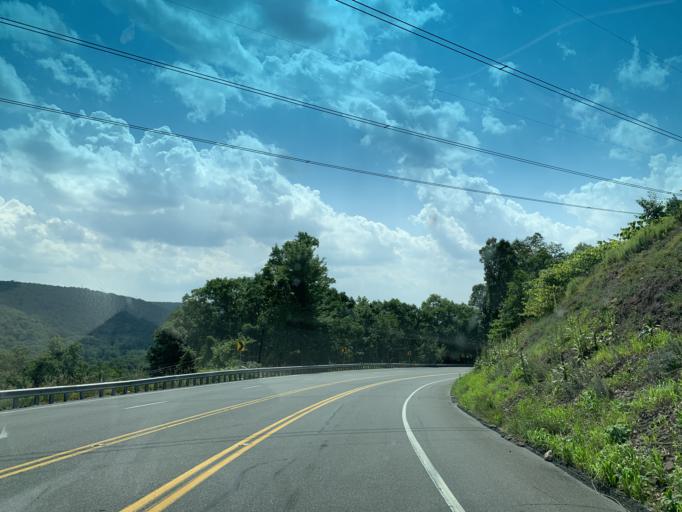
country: US
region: Pennsylvania
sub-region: Schuylkill County
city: Girardville
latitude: 40.7769
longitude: -76.2729
